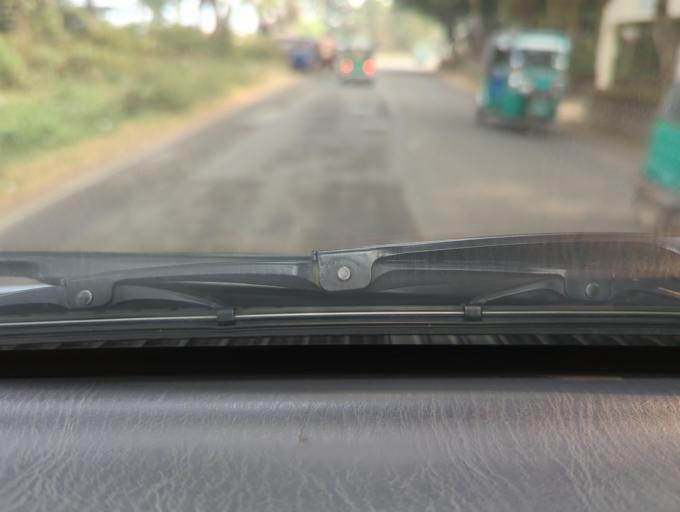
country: BD
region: Sylhet
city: Maulavi Bazar
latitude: 24.4966
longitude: 91.7444
